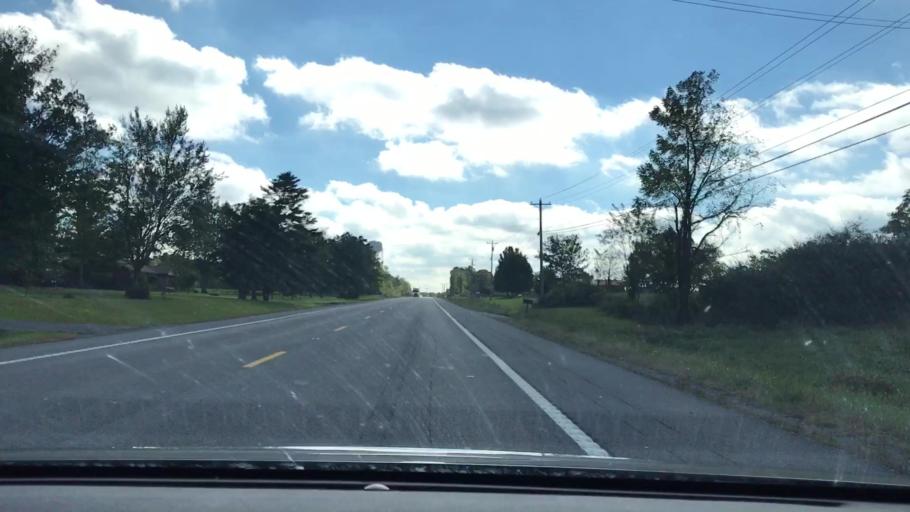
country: US
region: Tennessee
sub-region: Fentress County
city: Grimsley
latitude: 36.2498
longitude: -84.9961
